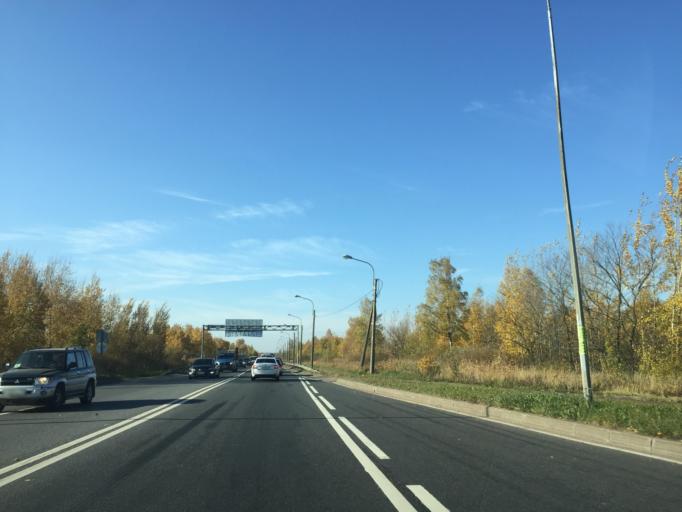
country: RU
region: St.-Petersburg
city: Metallostroy
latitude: 59.7483
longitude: 30.5266
